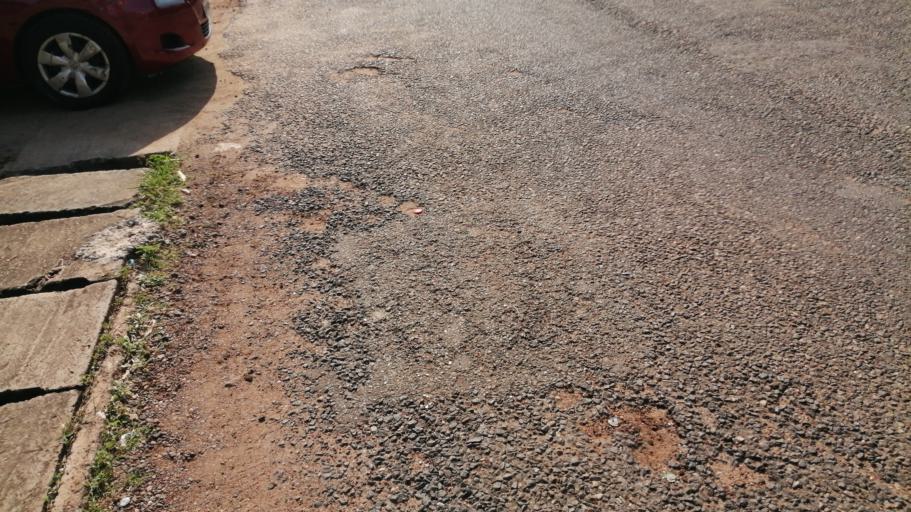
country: GH
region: Greater Accra
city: Medina Estates
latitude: 5.6178
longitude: -0.1823
